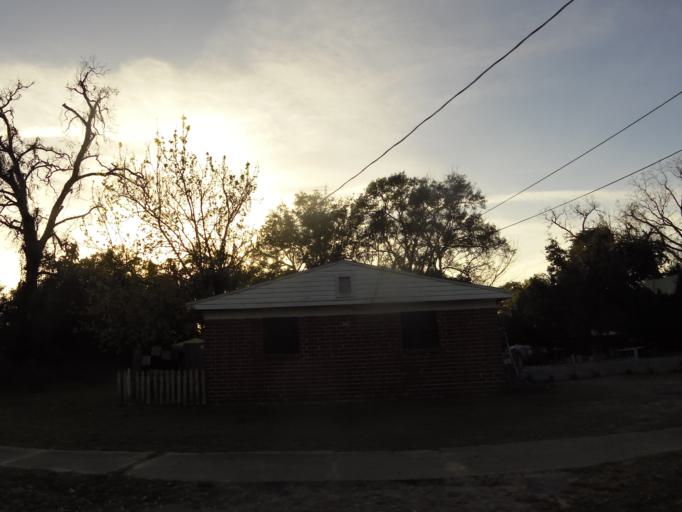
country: US
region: Florida
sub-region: Duval County
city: Jacksonville
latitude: 30.3373
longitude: -81.6403
